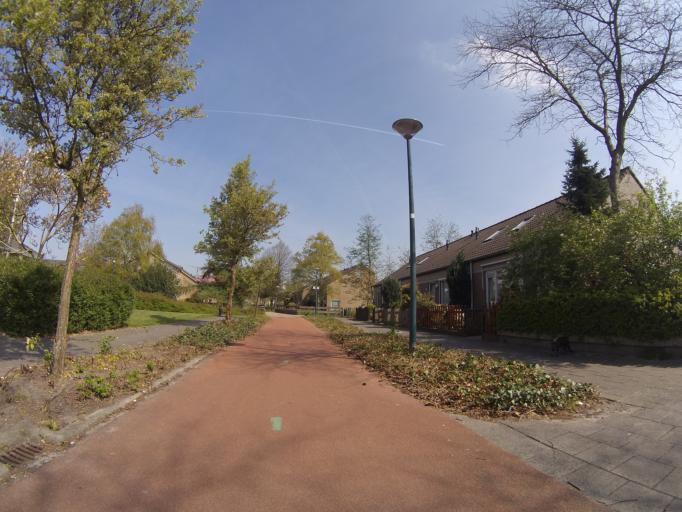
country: NL
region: North Holland
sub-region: Gemeente Blaricum
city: Blaricum
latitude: 52.2496
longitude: 5.2588
